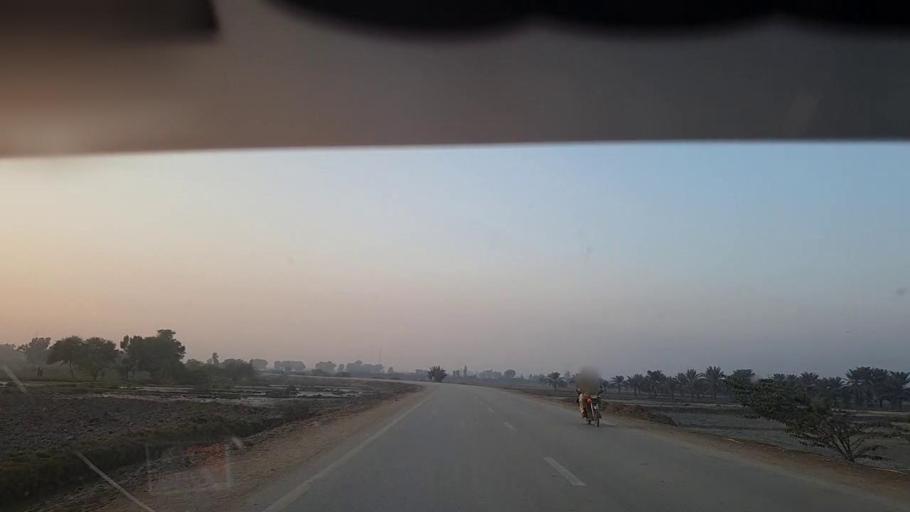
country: PK
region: Sindh
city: Ranipur
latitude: 27.2697
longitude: 68.5183
